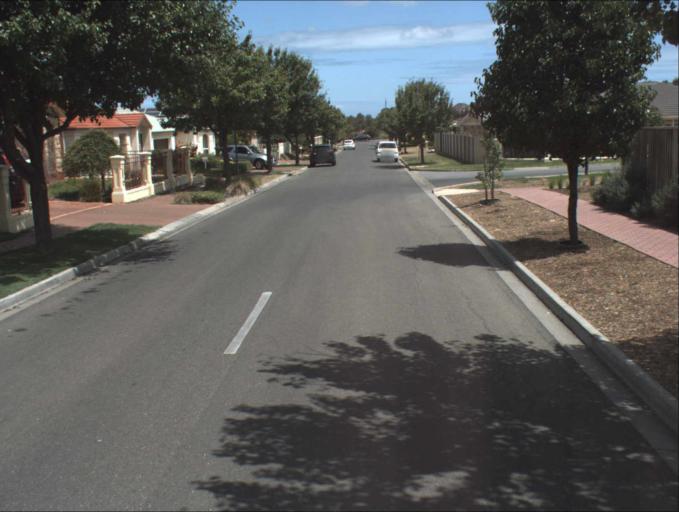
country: AU
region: South Australia
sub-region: Port Adelaide Enfield
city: Gilles Plains
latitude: -34.8543
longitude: 138.6318
